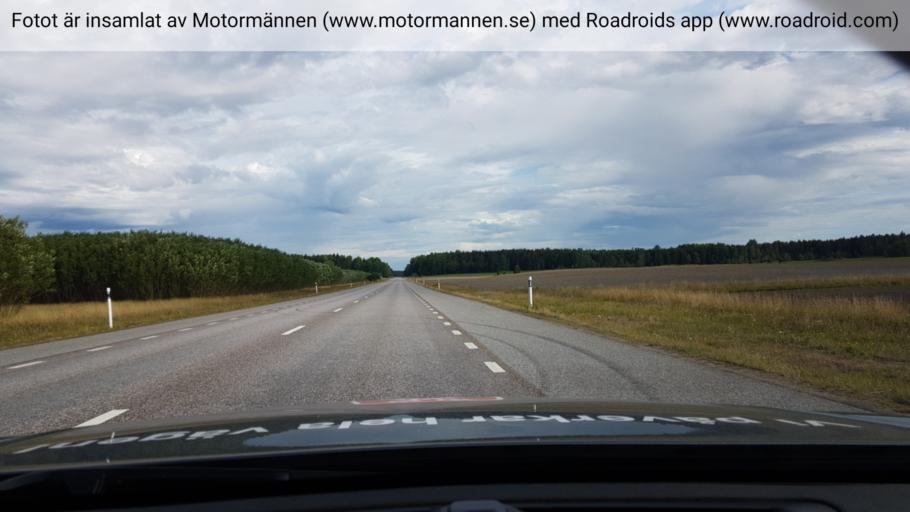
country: SE
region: Uppsala
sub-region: Heby Kommun
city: Morgongava
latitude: 59.8592
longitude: 16.9285
